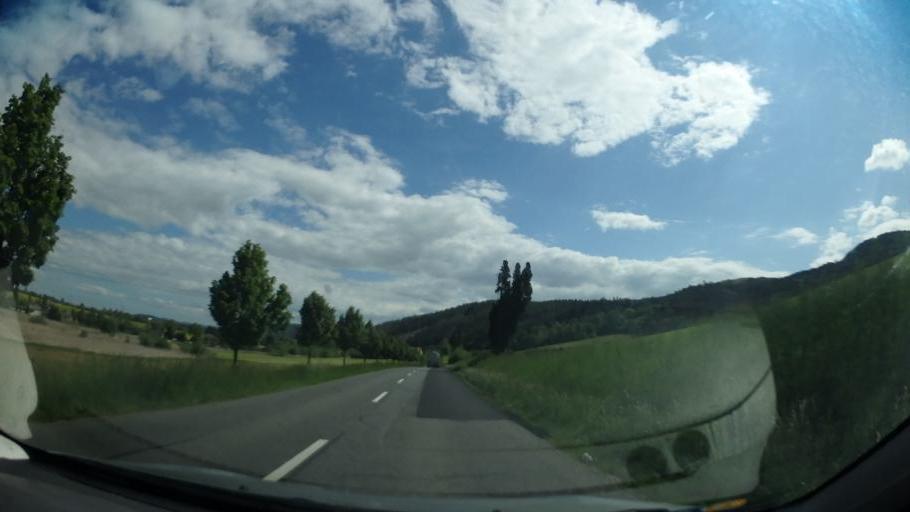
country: CZ
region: Pardubicky
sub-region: Okres Svitavy
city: Moravska Trebova
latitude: 49.7390
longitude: 16.6482
